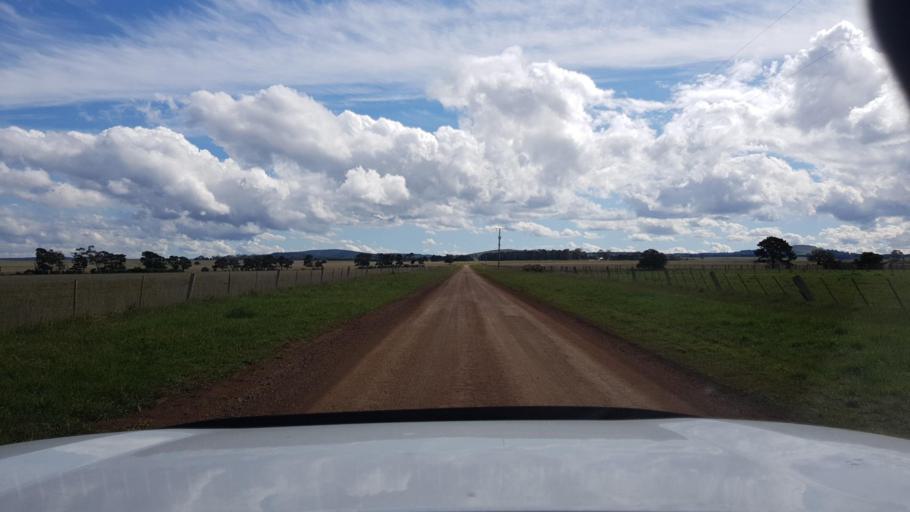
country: AU
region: Victoria
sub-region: Hume
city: Sunbury
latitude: -37.5924
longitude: 144.6714
